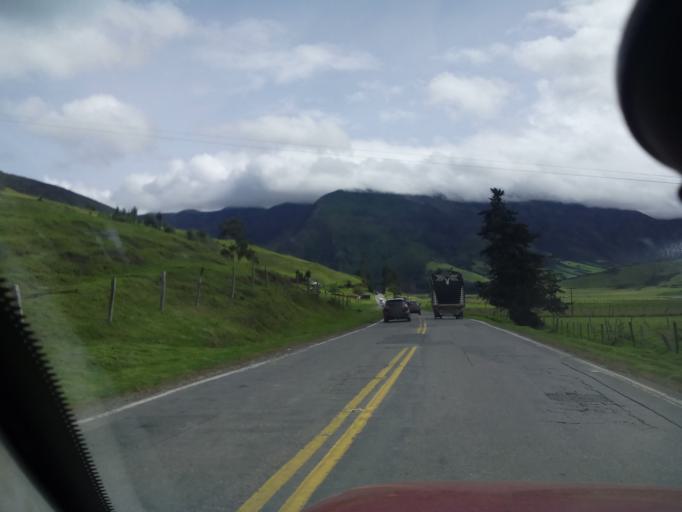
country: CO
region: Boyaca
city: Combita
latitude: 5.6945
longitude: -73.3682
